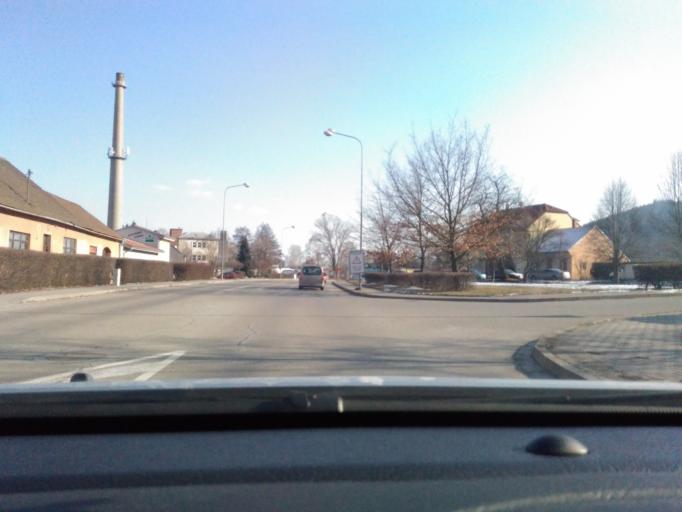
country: CZ
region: South Moravian
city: Predklasteri
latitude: 49.3527
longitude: 16.4062
